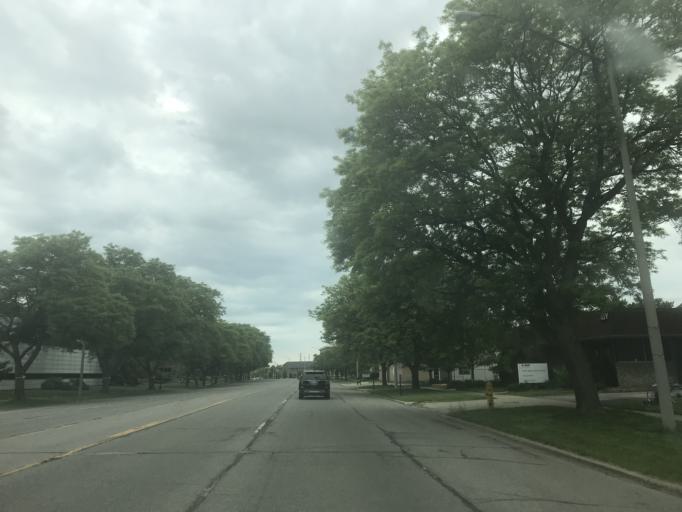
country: US
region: Michigan
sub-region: Wayne County
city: Wyandotte
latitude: 42.2207
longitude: -83.1504
